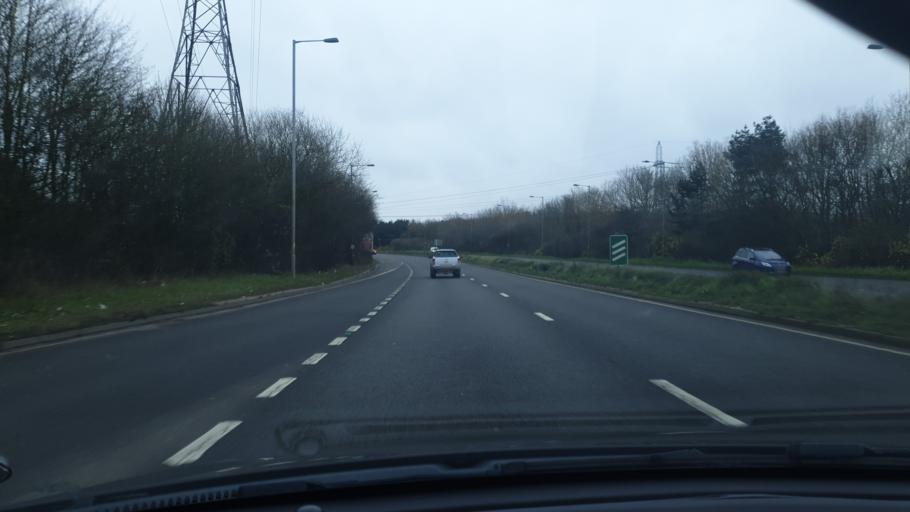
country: GB
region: England
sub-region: Walsall
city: Willenhall
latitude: 52.5762
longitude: -2.0525
